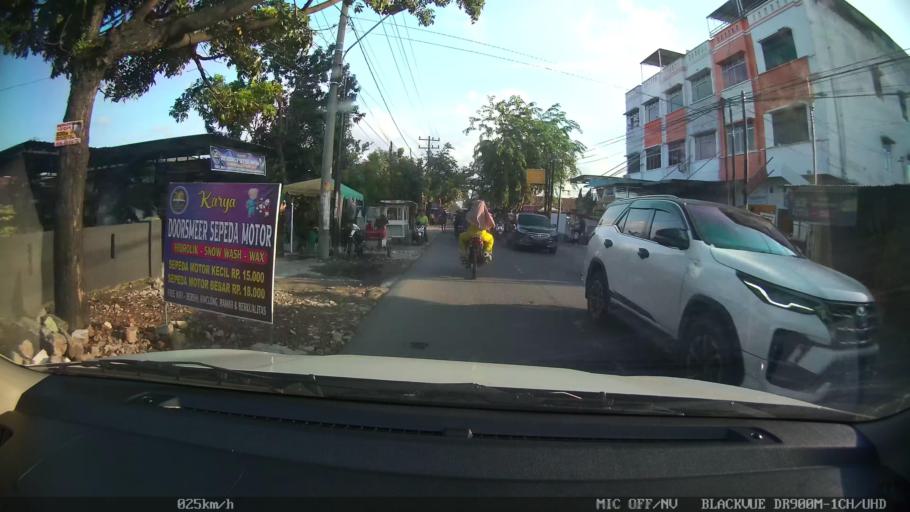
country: ID
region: North Sumatra
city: Medan
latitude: 3.6145
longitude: 98.6657
